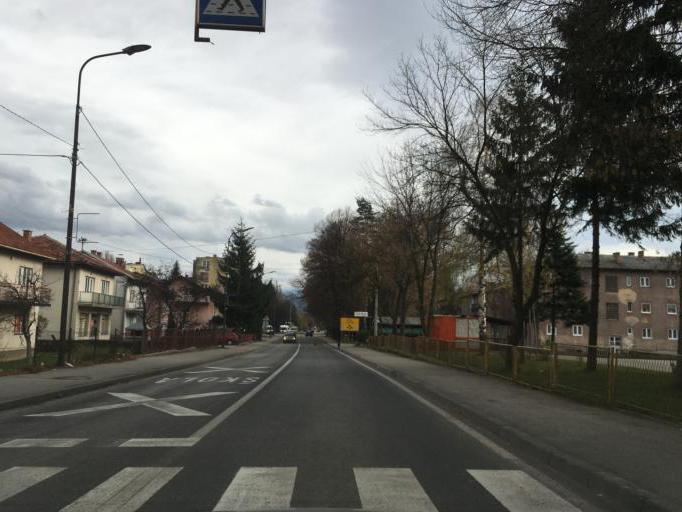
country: BA
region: Federation of Bosnia and Herzegovina
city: Bugojno
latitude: 44.0517
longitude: 17.4358
